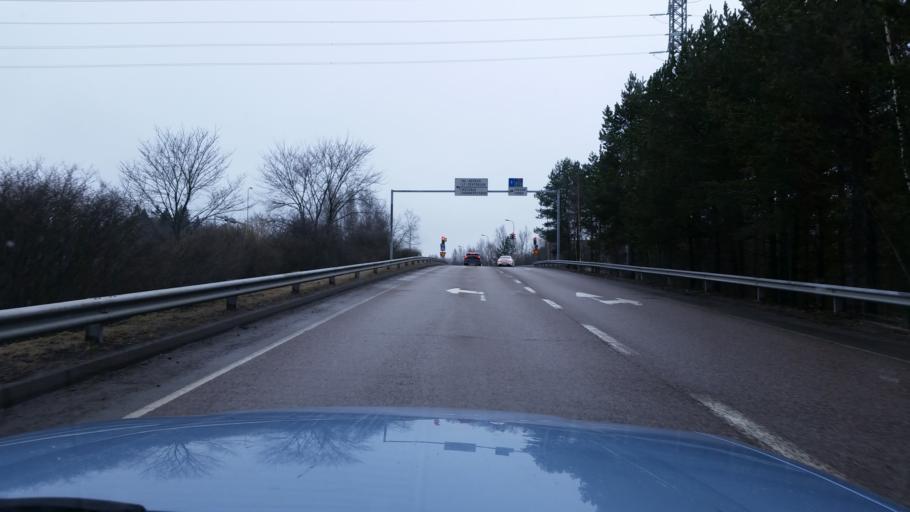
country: FI
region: Uusimaa
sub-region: Helsinki
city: Helsinki
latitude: 60.2207
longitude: 24.9088
